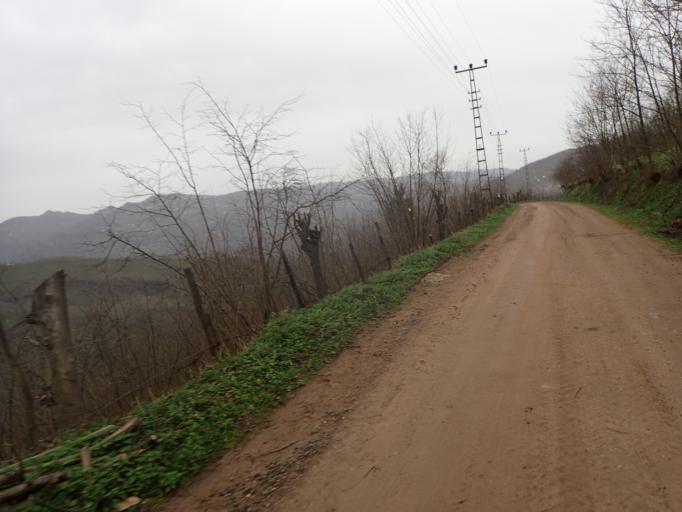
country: TR
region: Ordu
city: Camas
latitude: 40.8866
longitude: 37.4970
